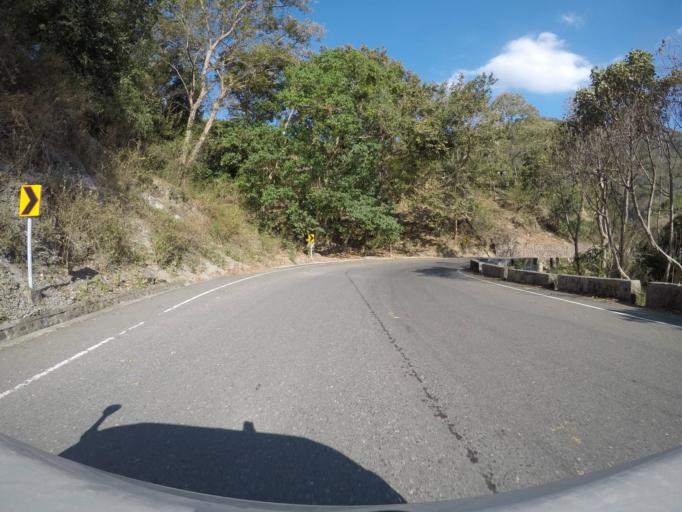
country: TL
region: Liquica
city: Maubara
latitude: -8.6744
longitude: 125.1097
